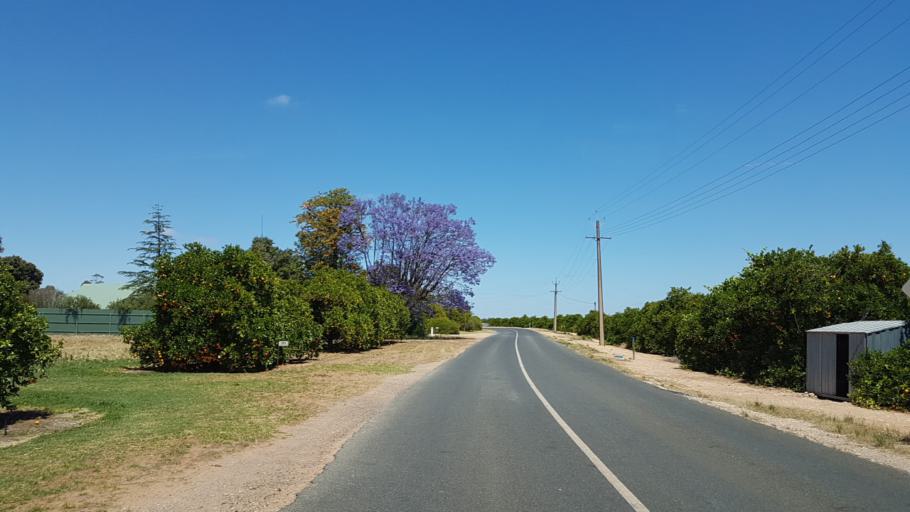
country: AU
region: South Australia
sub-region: Loxton Waikerie
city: Waikerie
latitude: -34.1755
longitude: 140.0290
